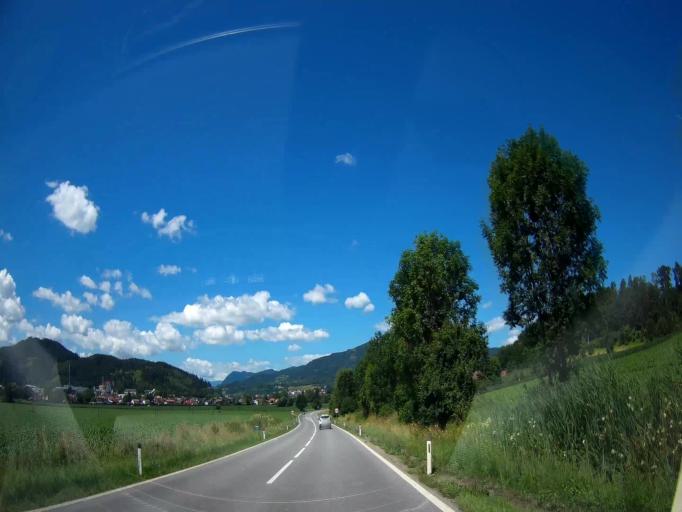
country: AT
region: Carinthia
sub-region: Politischer Bezirk Sankt Veit an der Glan
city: Sankt Veit an der Glan
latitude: 46.7631
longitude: 14.3904
